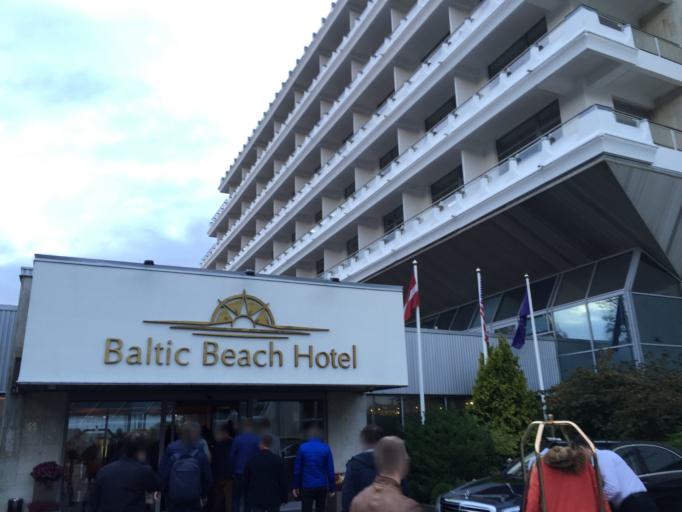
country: LV
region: Jurmala
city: Jurmala
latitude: 56.9755
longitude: 23.7974
